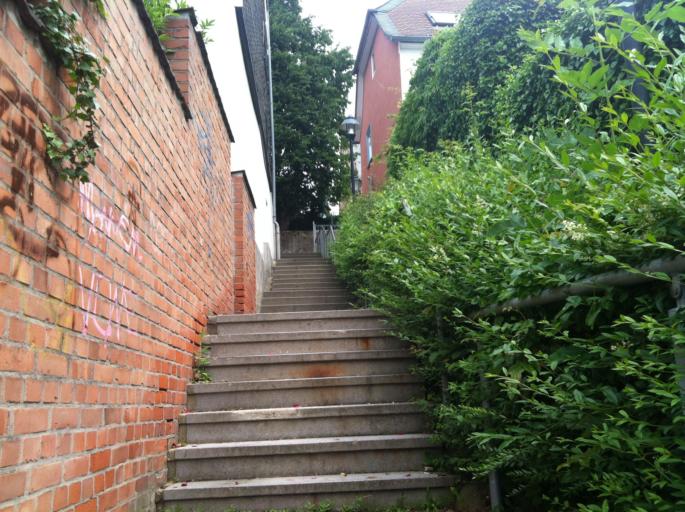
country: DE
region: Hesse
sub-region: Regierungsbezirk Darmstadt
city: Bad Homburg vor der Hoehe
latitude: 50.2255
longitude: 8.6128
